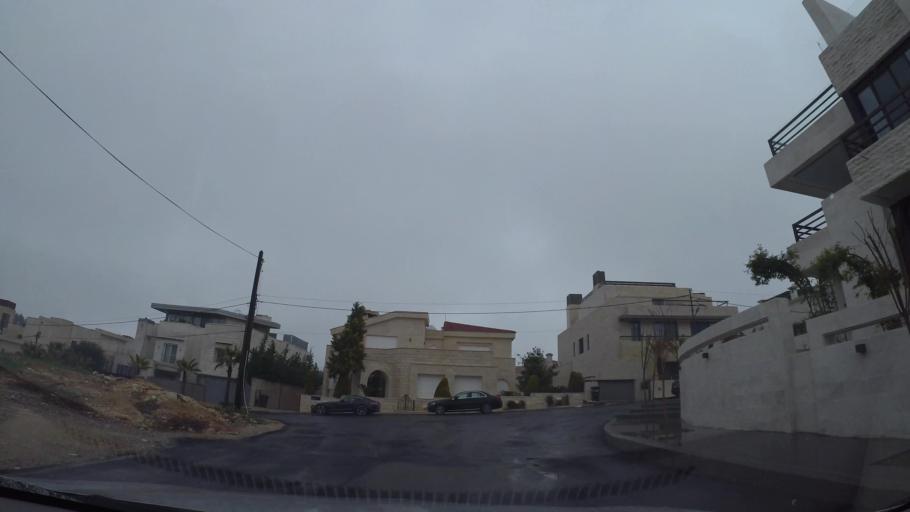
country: JO
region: Amman
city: Al Jubayhah
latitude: 32.0067
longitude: 35.8254
